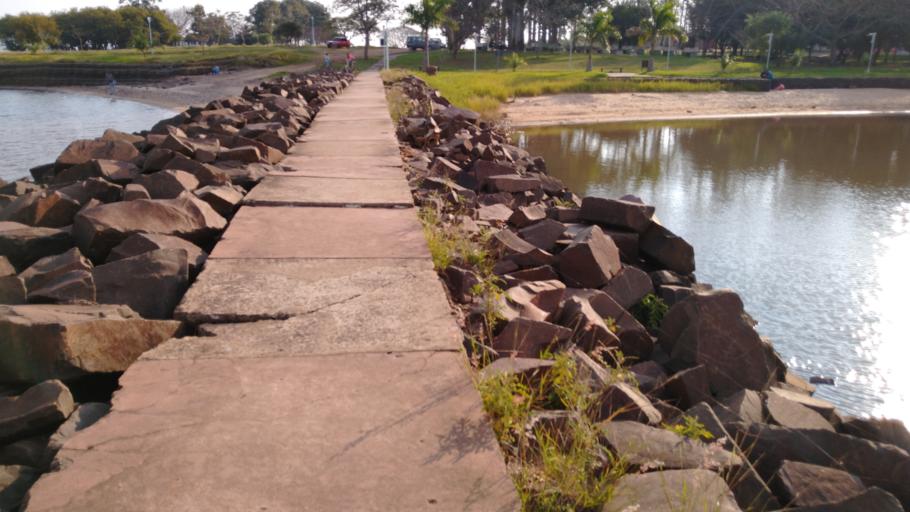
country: AR
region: Entre Rios
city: Santa Ana
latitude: -30.9141
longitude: -57.9247
